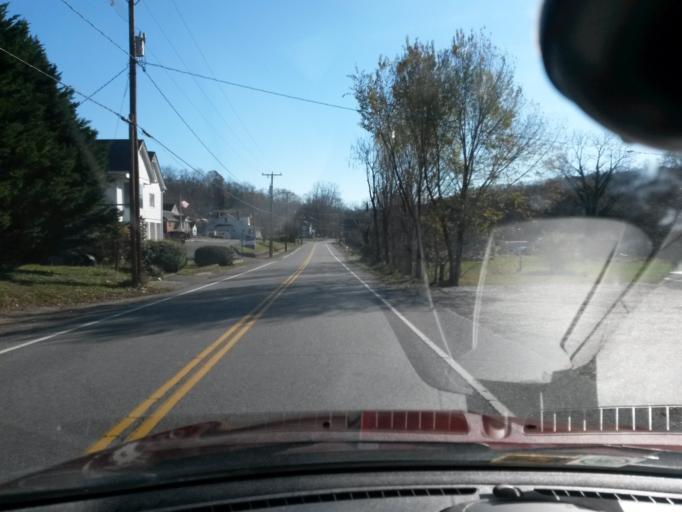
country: US
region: Virginia
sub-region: Botetourt County
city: Fincastle
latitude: 37.6399
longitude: -79.8002
